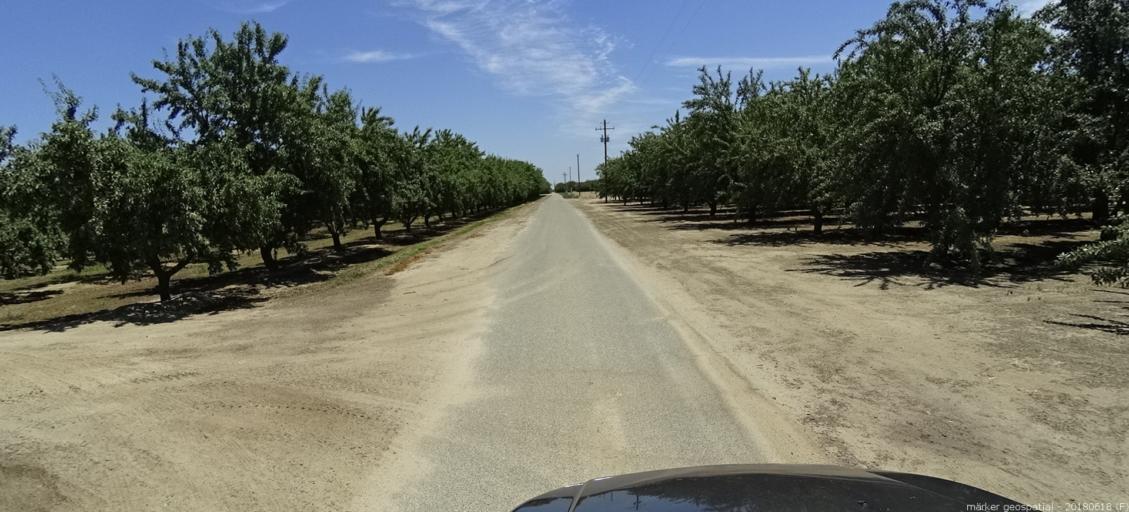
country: US
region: California
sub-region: Madera County
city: Madera
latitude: 36.9056
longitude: -120.1412
